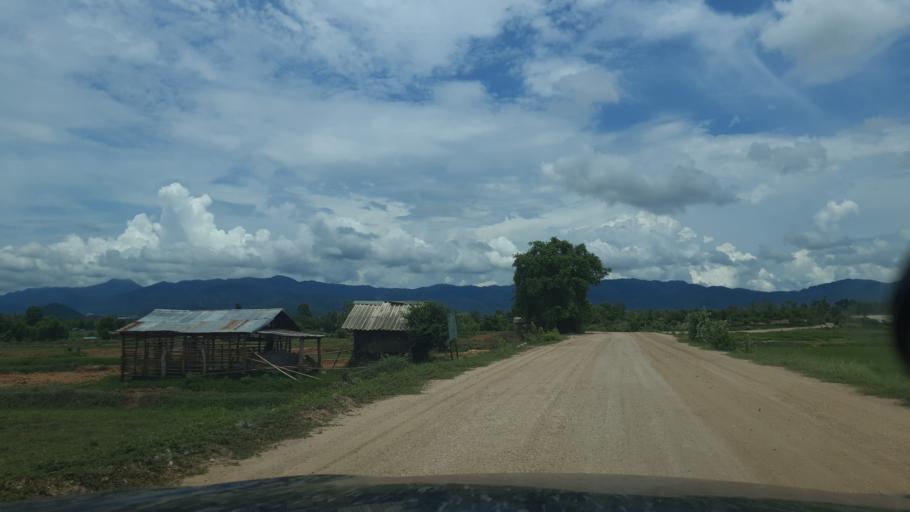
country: TH
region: Lampang
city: Sop Prap
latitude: 17.9379
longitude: 99.3613
